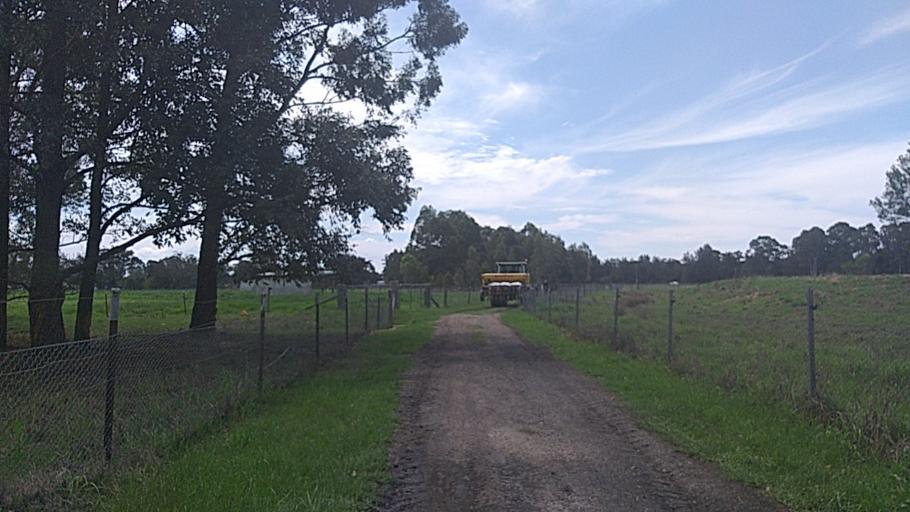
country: AU
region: New South Wales
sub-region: Hawkesbury
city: Richmond
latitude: -33.6105
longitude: 150.7579
